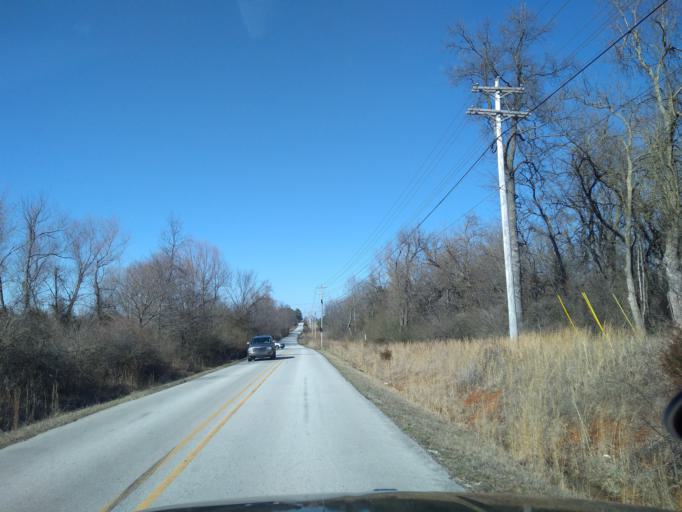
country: US
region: Arkansas
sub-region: Washington County
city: Farmington
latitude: 36.0599
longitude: -94.2402
